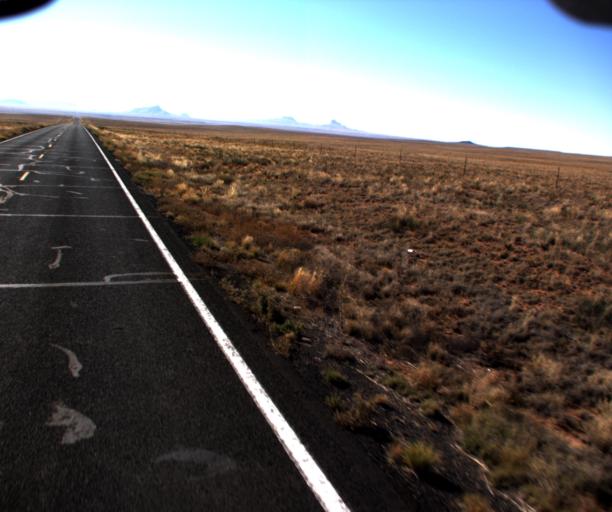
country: US
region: Arizona
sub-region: Navajo County
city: First Mesa
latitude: 35.6335
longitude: -110.4831
